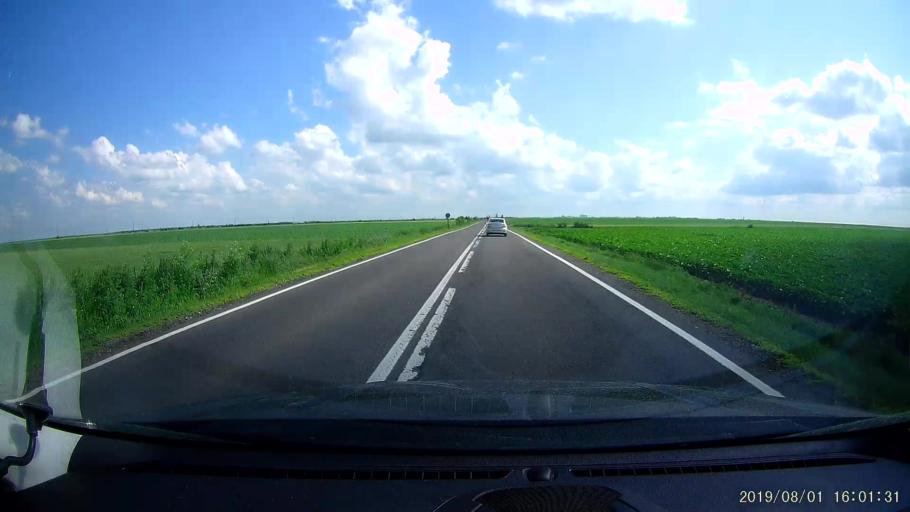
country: RO
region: Ialomita
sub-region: Comuna Ciulnita
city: Ciulnita
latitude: 44.5066
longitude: 27.3901
